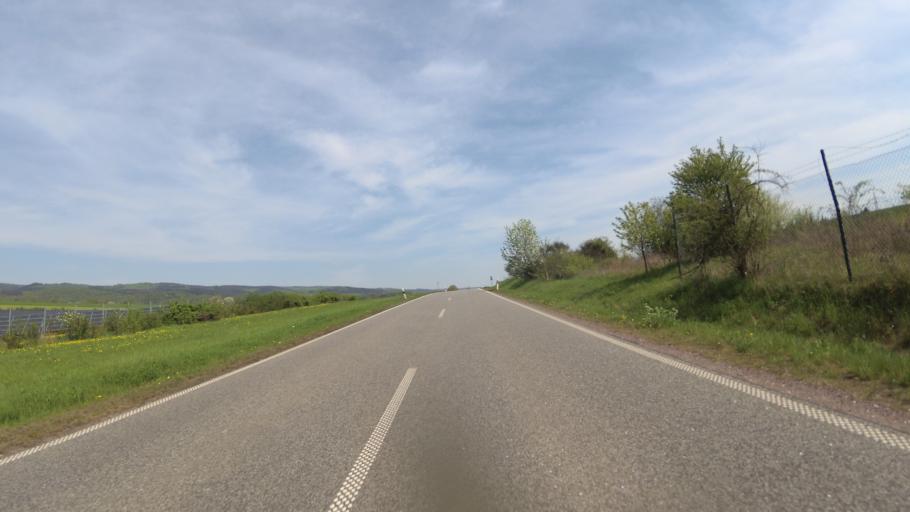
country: DE
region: Rheinland-Pfalz
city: Kinderbeuern
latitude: 50.0033
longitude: 7.0142
